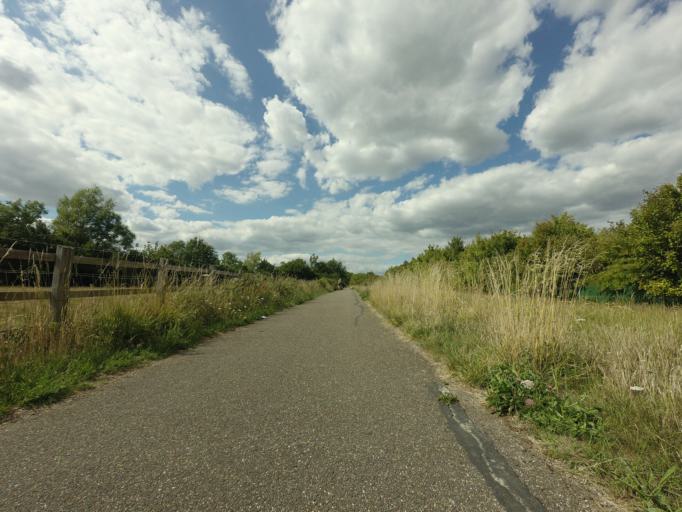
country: GB
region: England
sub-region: East Sussex
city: Eastbourne
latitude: 50.8142
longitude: 0.2762
